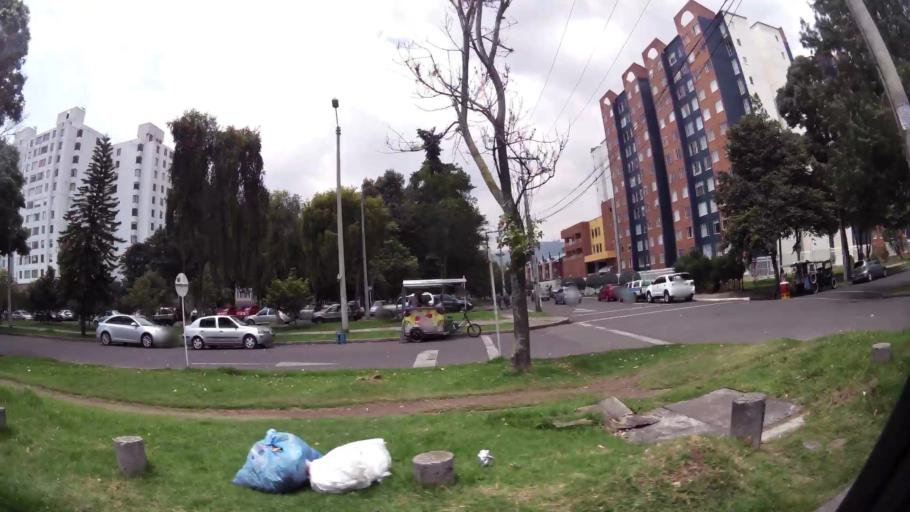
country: CO
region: Cundinamarca
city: La Calera
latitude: 4.7389
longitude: -74.0346
